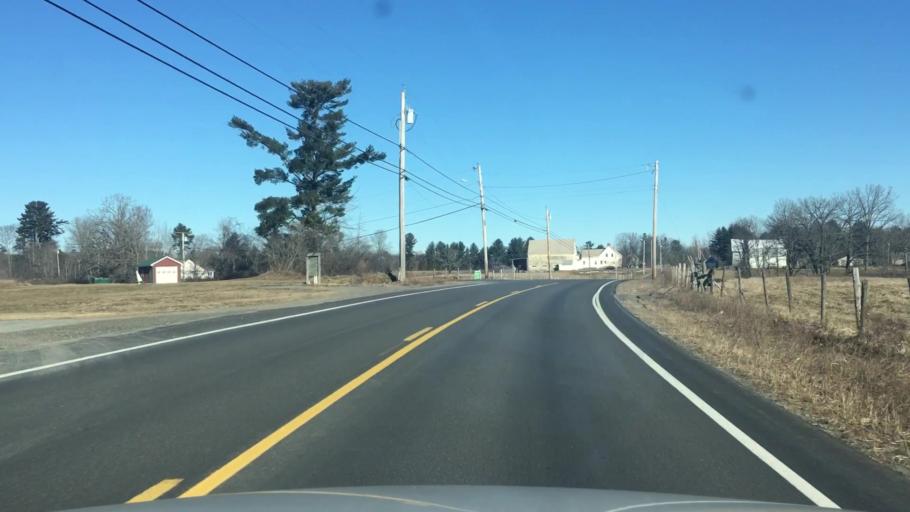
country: US
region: Maine
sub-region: Kennebec County
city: Benton
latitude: 44.5989
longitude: -69.5430
